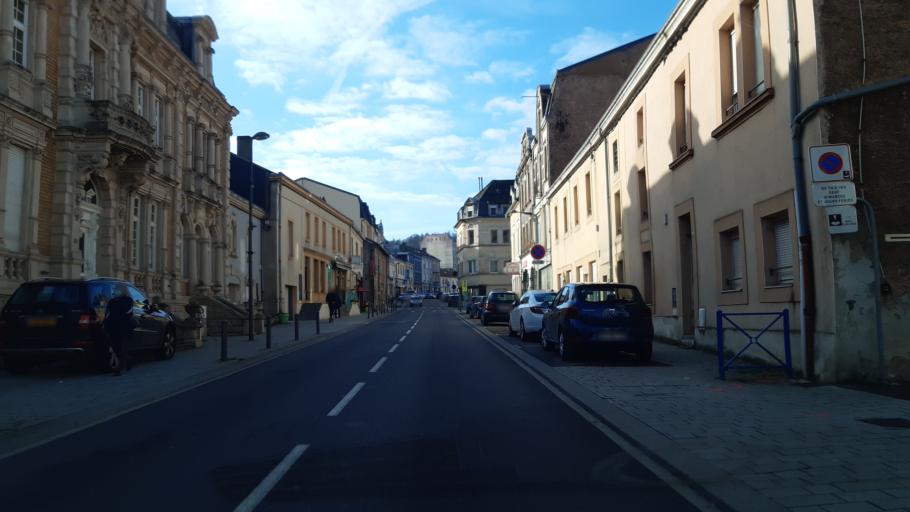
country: FR
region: Lorraine
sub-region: Departement de la Moselle
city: Audun-le-Tiche
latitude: 49.4710
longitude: 5.9572
